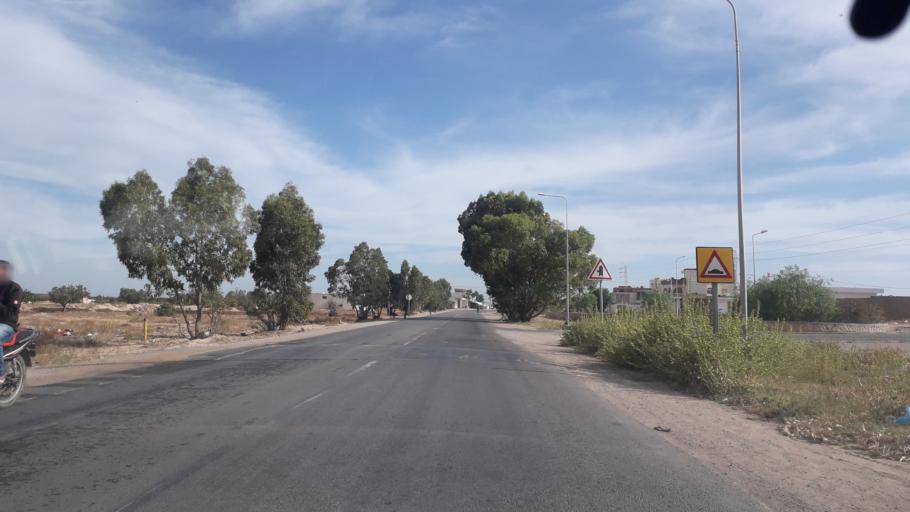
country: TN
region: Safaqis
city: Al Qarmadah
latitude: 34.8882
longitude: 10.7625
